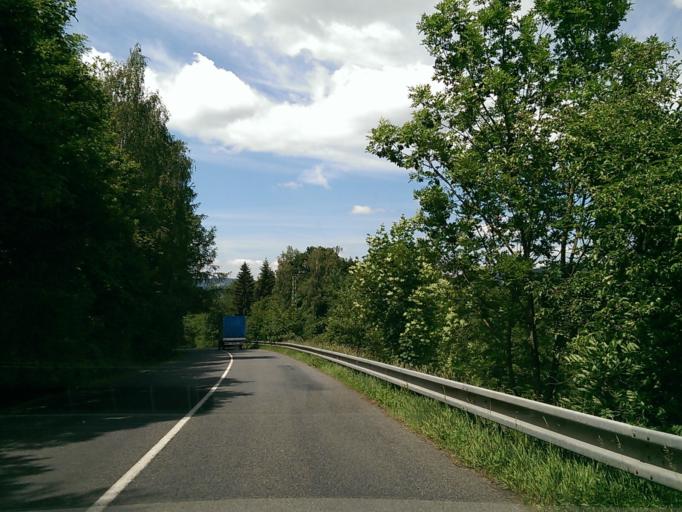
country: CZ
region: Liberecky
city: Zelezny Brod
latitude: 50.6366
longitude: 15.2757
